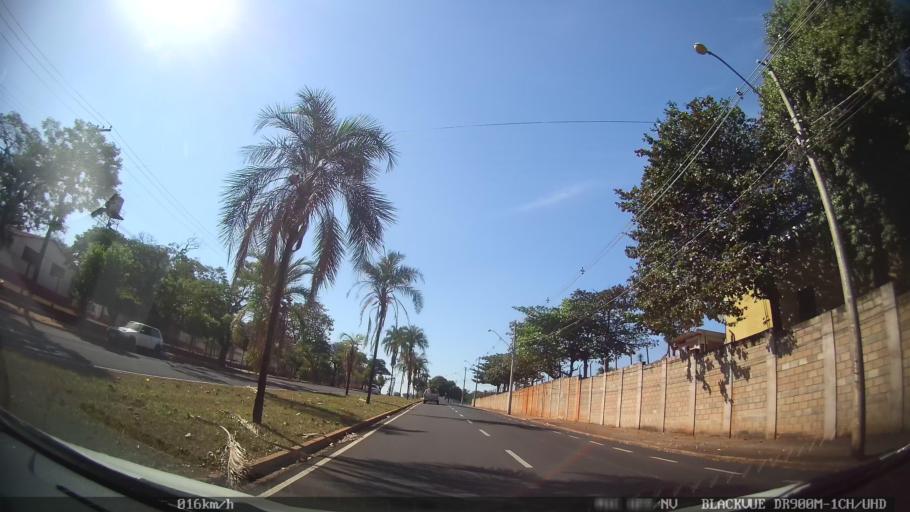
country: BR
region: Sao Paulo
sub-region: Sao Jose Do Rio Preto
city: Sao Jose do Rio Preto
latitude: -20.8106
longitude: -49.4125
